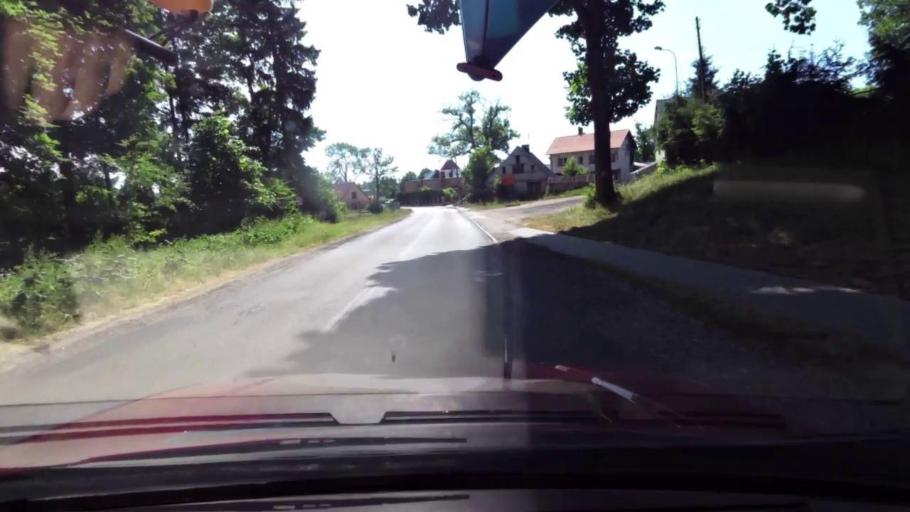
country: PL
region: Pomeranian Voivodeship
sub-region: Powiat slupski
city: Kobylnica
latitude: 54.3897
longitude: 16.9769
